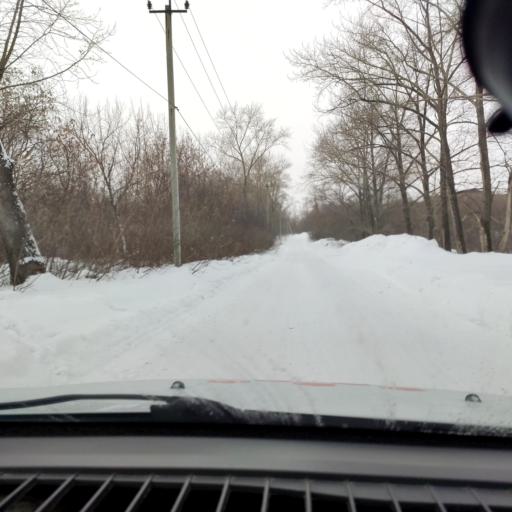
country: RU
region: Bashkortostan
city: Blagoveshchensk
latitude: 54.8991
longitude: 56.0623
